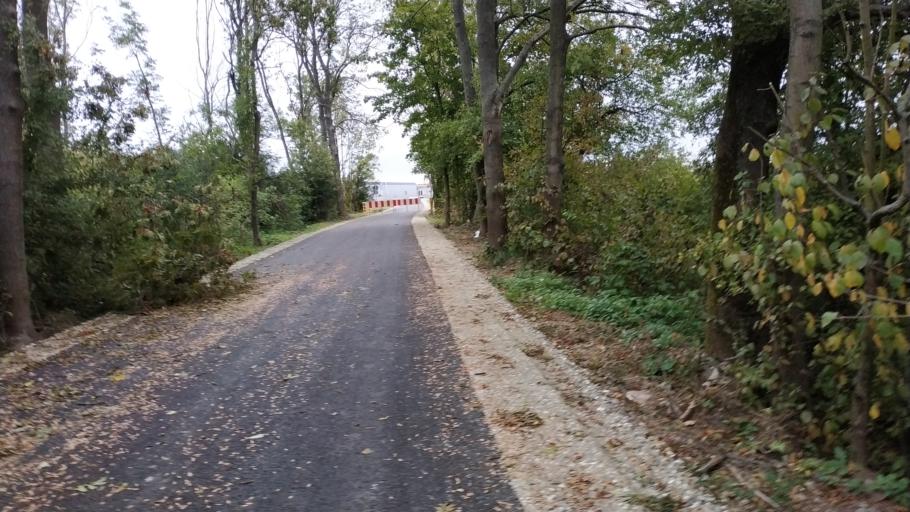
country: PL
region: Lower Silesian Voivodeship
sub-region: Powiat wroclawski
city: Bielany Wroclawskie
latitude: 51.0293
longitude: 16.9500
